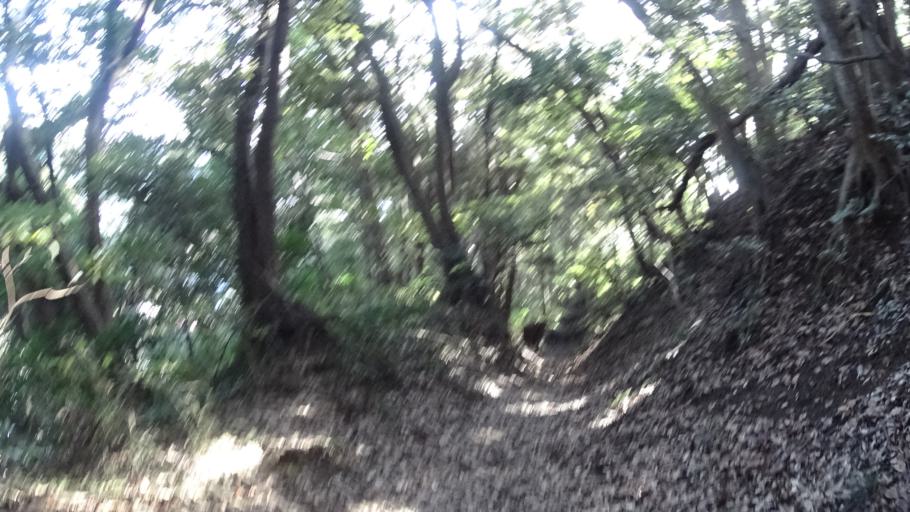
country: JP
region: Kanagawa
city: Hayama
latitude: 35.2717
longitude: 139.5893
